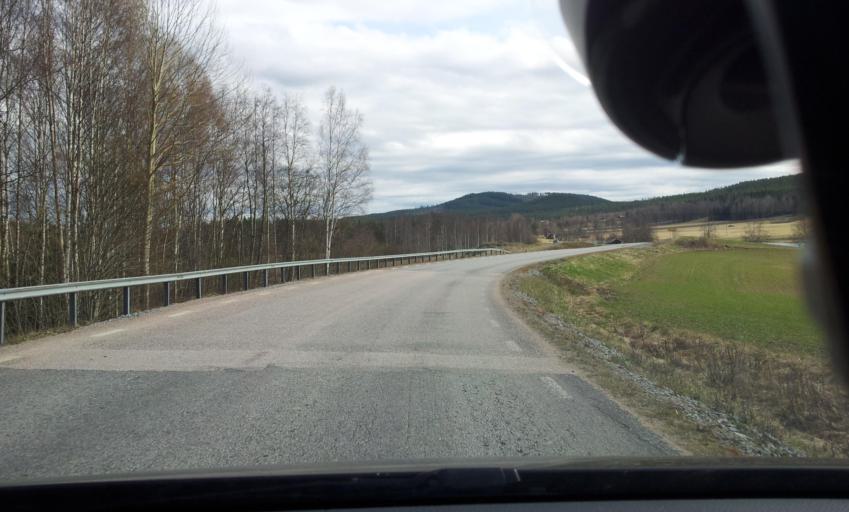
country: SE
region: Gaevleborg
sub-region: Ljusdals Kommun
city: Farila
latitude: 61.7745
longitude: 15.9556
